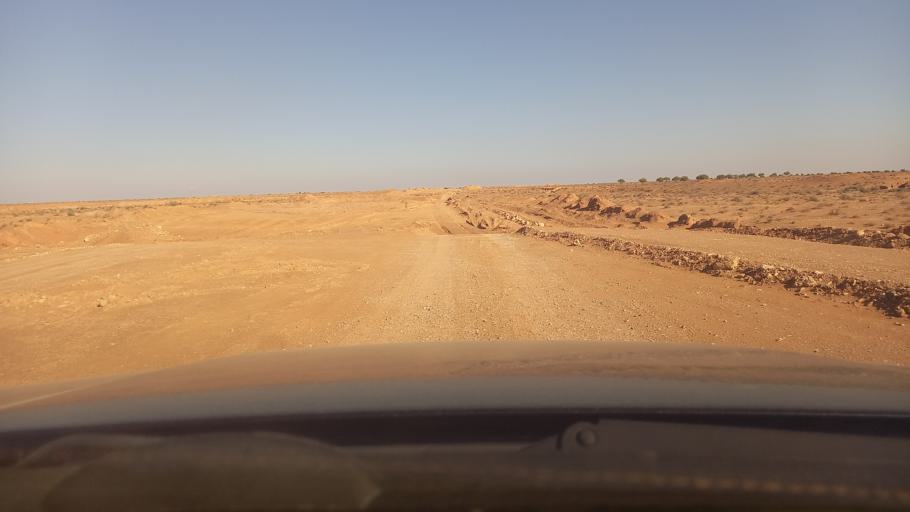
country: TN
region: Madanin
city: Medenine
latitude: 33.1461
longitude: 10.5066
